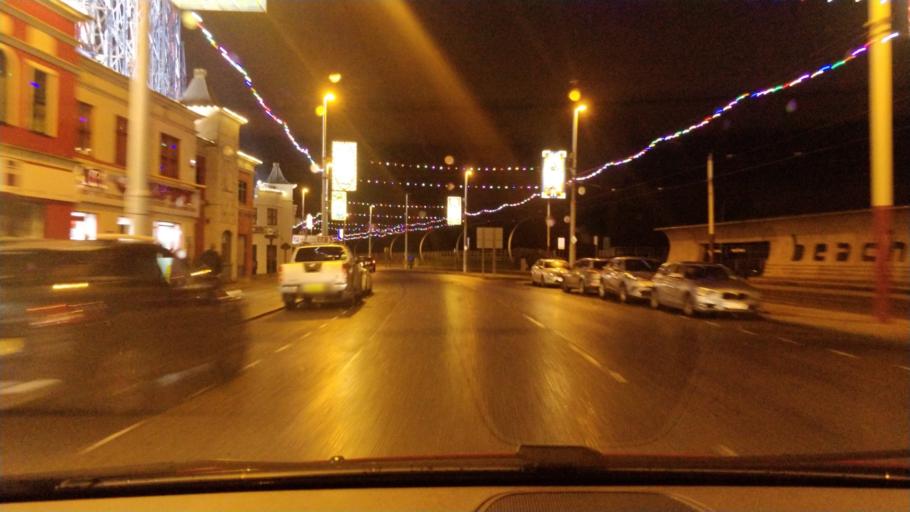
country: GB
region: England
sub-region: Blackpool
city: Blackpool
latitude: 53.7913
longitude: -3.0575
